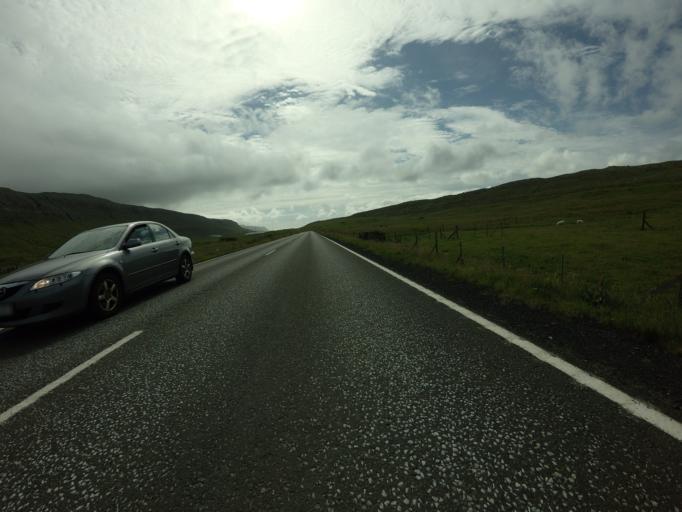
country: FO
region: Sandoy
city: Sandur
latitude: 61.8611
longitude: -6.8355
